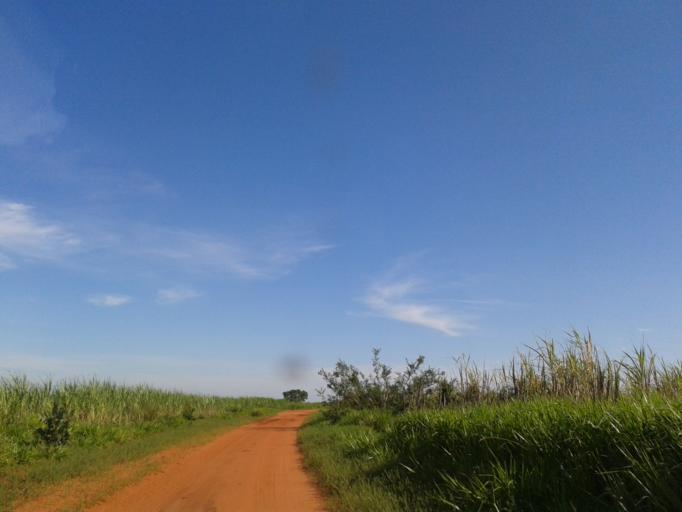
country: BR
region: Minas Gerais
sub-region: Santa Vitoria
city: Santa Vitoria
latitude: -19.1034
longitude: -49.9911
